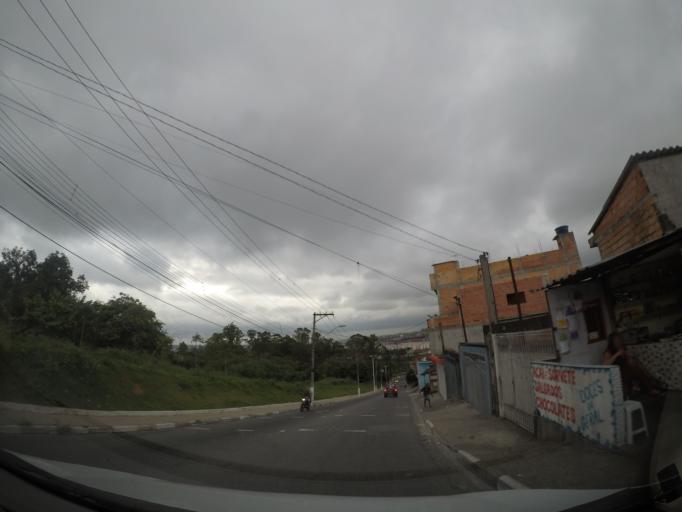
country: BR
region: Sao Paulo
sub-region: Aruja
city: Aruja
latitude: -23.4000
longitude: -46.4225
